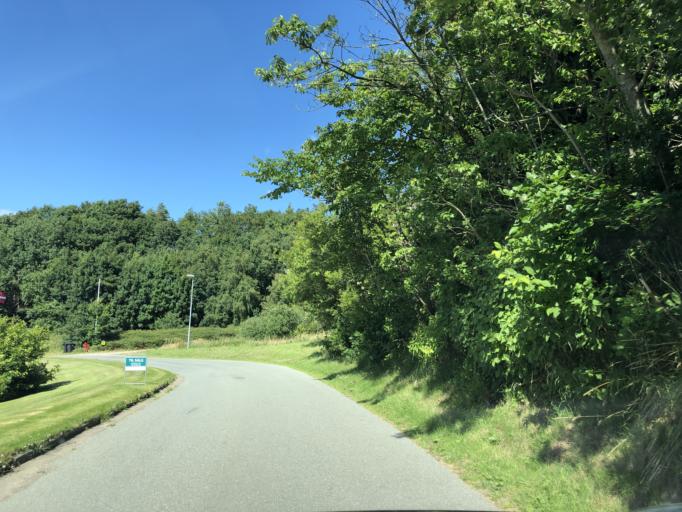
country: DK
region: Central Jutland
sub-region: Viborg Kommune
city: Stoholm
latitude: 56.4373
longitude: 9.1314
